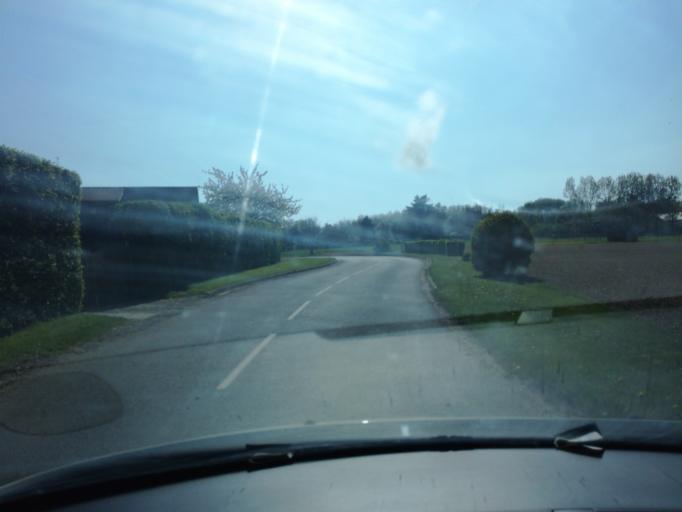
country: FR
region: Picardie
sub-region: Departement de la Somme
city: Poix-de-Picardie
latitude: 49.8227
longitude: 2.0196
